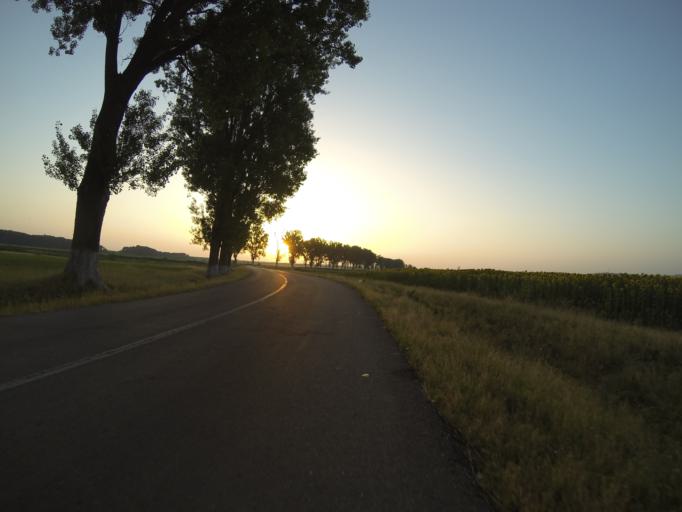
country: RO
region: Dolj
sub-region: Comuna Dobresti
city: Dobresti
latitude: 43.9822
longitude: 23.9179
